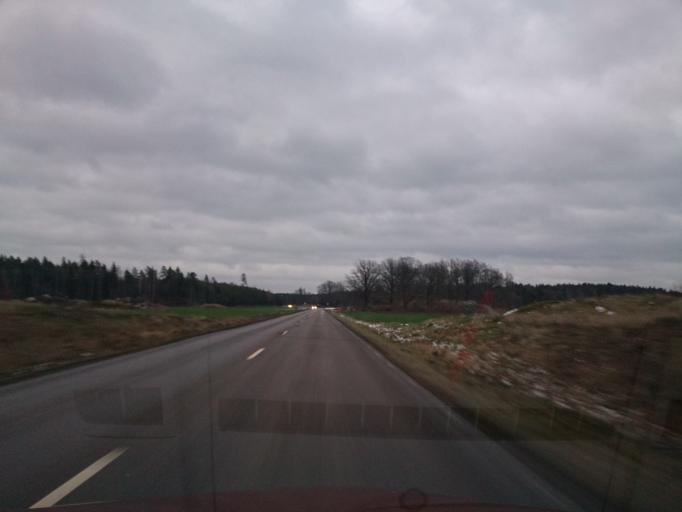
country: SE
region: OEstergoetland
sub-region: Linkopings Kommun
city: Linghem
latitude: 58.4027
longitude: 15.8041
